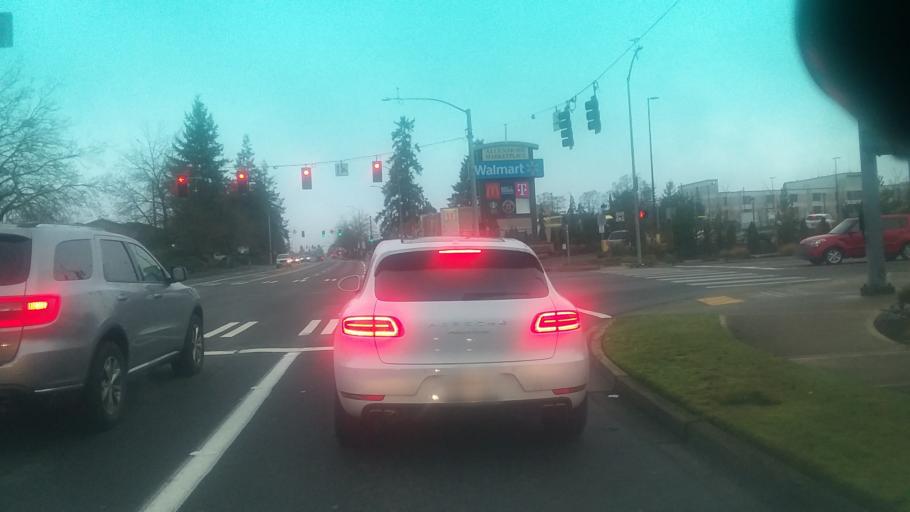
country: US
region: Washington
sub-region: Pierce County
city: Fircrest
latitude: 47.2389
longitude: -122.4818
